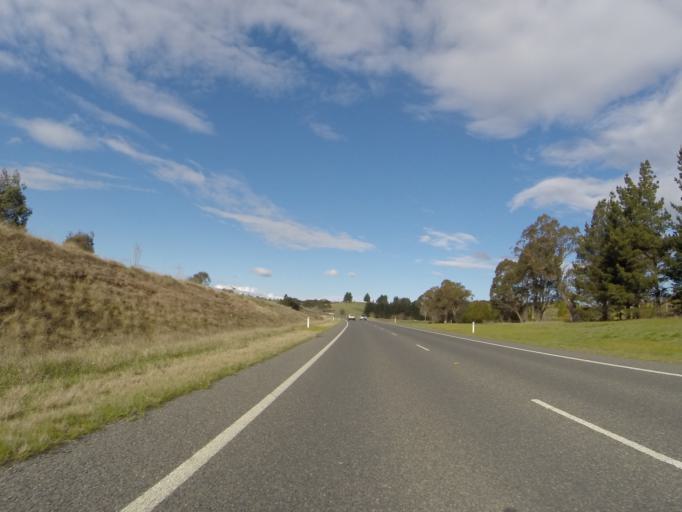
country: AU
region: New South Wales
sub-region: Wingecarribee
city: Bundanoon
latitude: -34.5865
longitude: 150.2667
